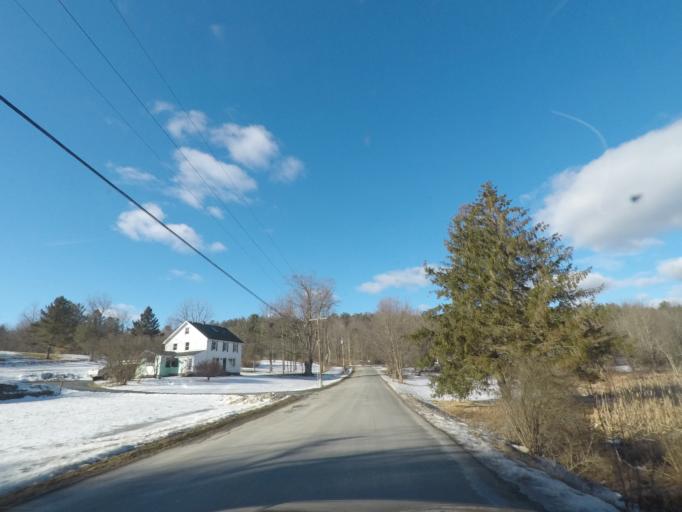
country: US
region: New York
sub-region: Rensselaer County
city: Averill Park
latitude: 42.5548
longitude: -73.5261
